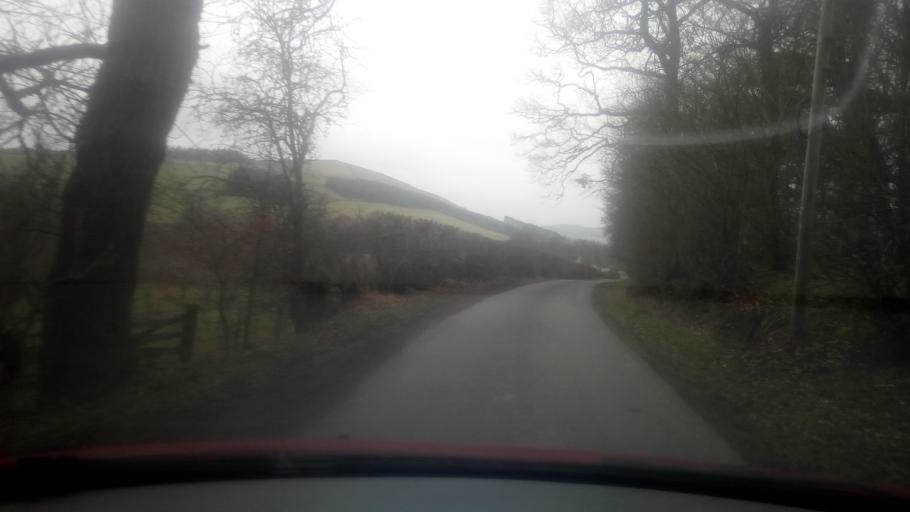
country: GB
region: Scotland
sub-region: The Scottish Borders
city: Jedburgh
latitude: 55.4144
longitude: -2.6472
